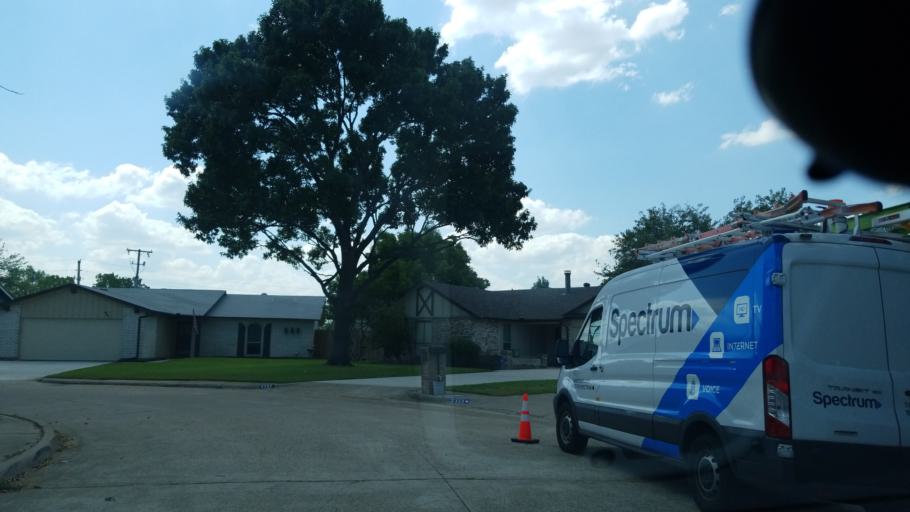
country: US
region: Texas
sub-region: Dallas County
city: Grand Prairie
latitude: 32.7112
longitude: -96.9923
